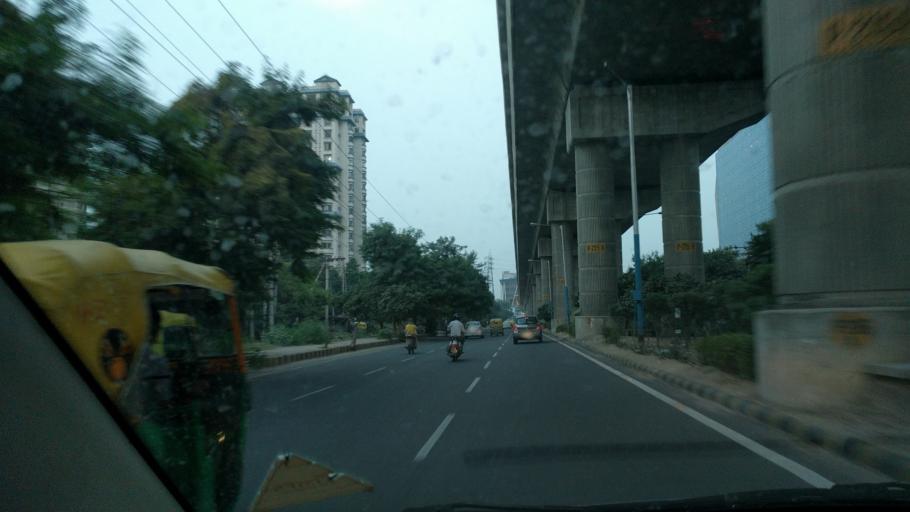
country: IN
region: Haryana
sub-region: Gurgaon
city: Gurgaon
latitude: 28.4547
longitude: 77.0685
